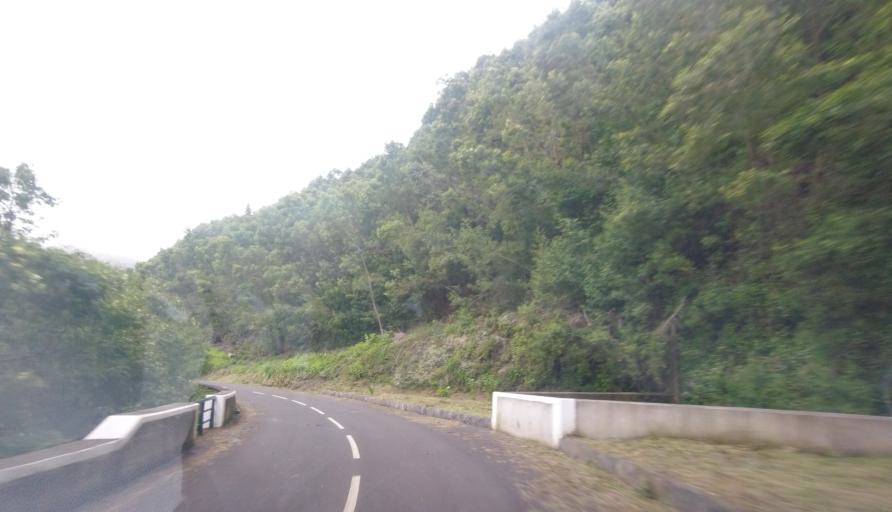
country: PT
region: Madeira
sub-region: Funchal
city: Nossa Senhora do Monte
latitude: 32.6917
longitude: -16.8929
